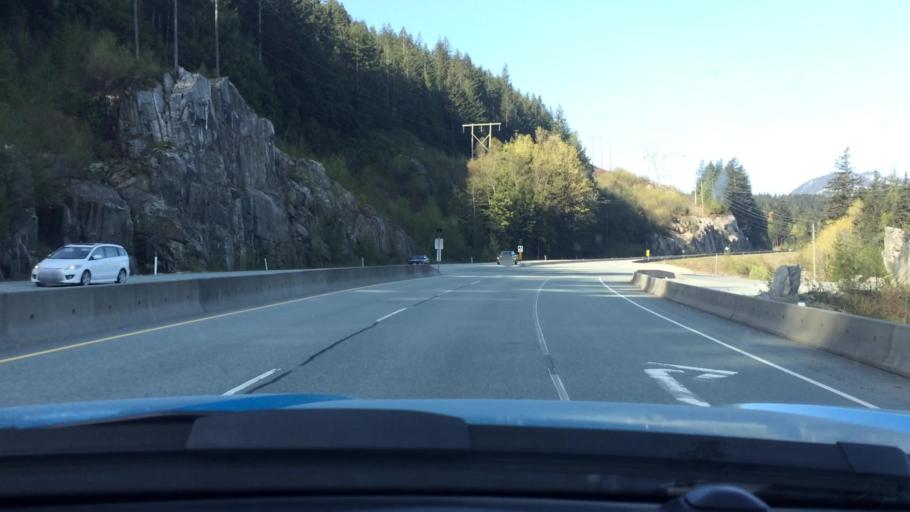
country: CA
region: British Columbia
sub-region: Greater Vancouver Regional District
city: Lions Bay
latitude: 49.6548
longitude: -123.1897
